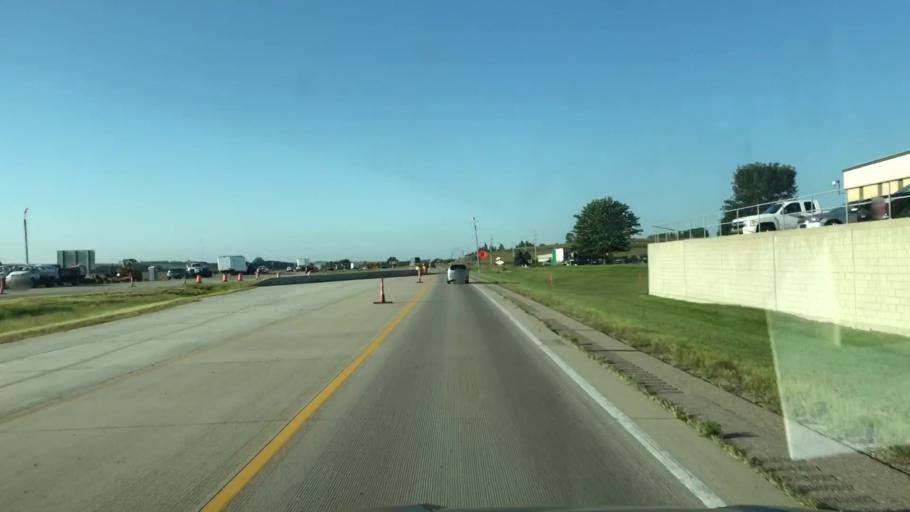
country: US
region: Iowa
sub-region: Plymouth County
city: Le Mars
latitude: 42.7491
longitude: -96.2120
